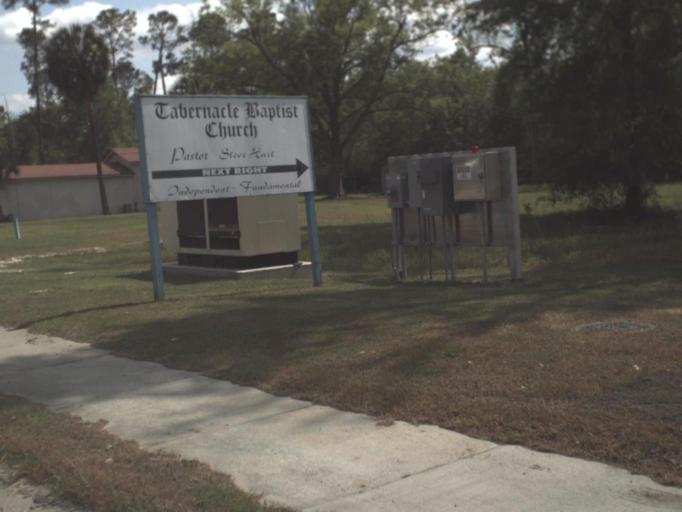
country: US
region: Alabama
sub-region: Escambia County
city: Flomaton
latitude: 30.9943
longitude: -87.2583
